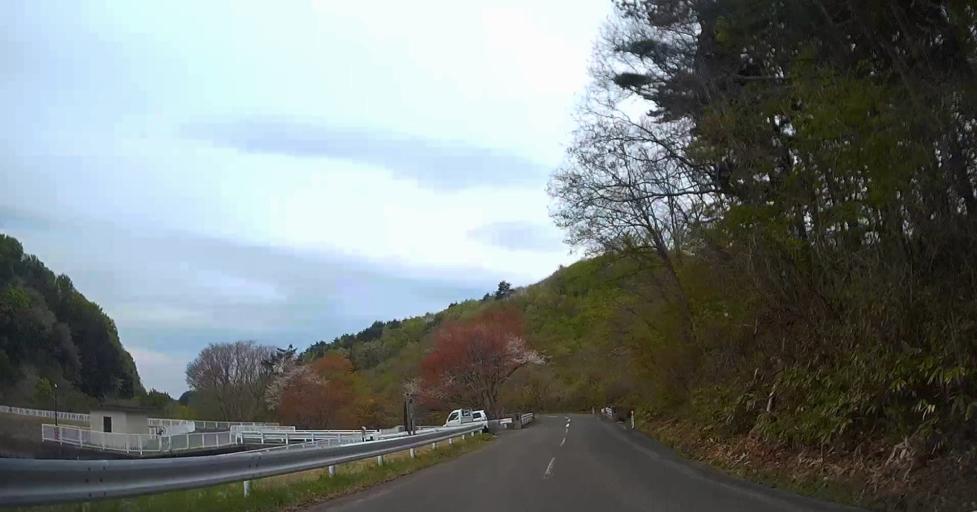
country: JP
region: Aomori
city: Goshogawara
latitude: 40.9045
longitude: 140.5078
